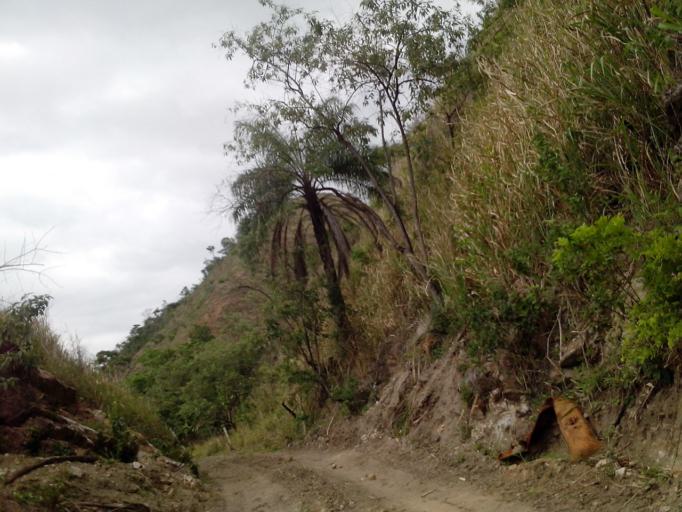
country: BR
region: Rio de Janeiro
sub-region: Miguel Pereira
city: Miguel Pereira
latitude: -22.5031
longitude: -43.5027
